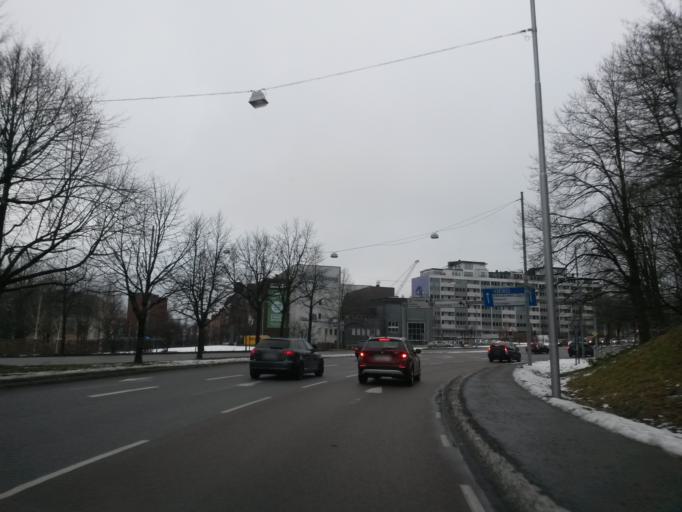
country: SE
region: Vaestra Goetaland
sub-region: Boras Kommun
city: Boras
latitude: 57.7165
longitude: 12.9447
